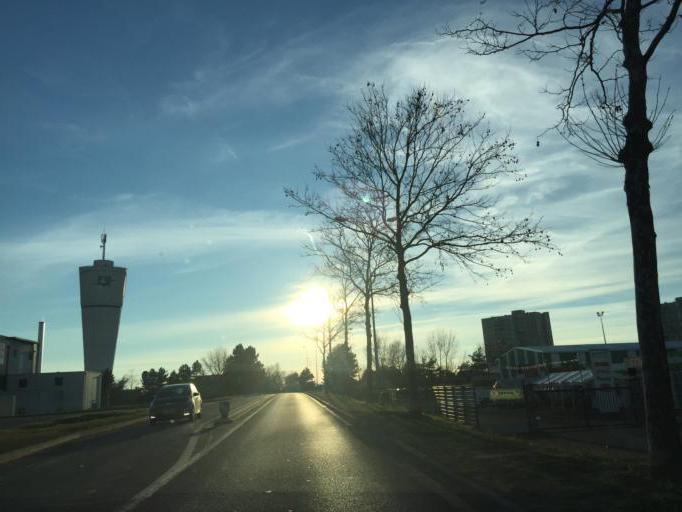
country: FR
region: Rhone-Alpes
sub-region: Departement de la Loire
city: Andrezieux-Boutheon
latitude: 45.5275
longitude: 4.2760
